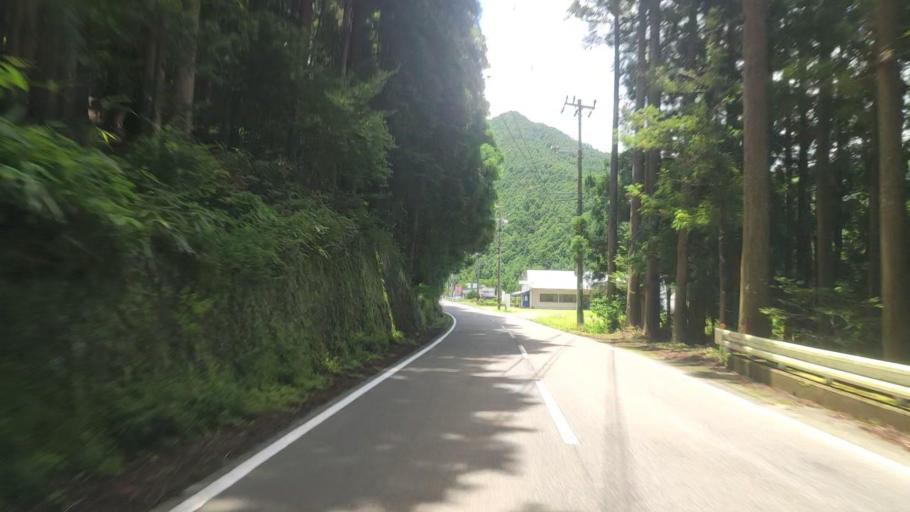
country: JP
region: Mie
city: Owase
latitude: 33.9667
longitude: 136.0612
